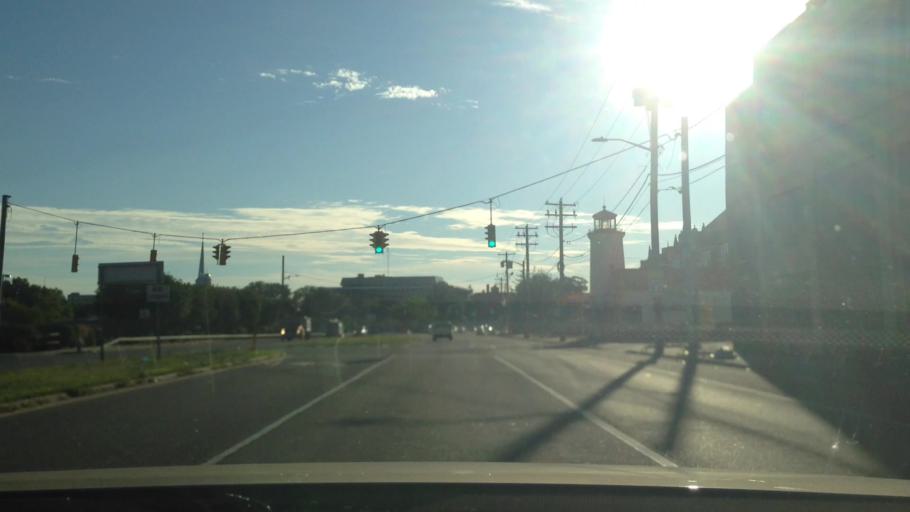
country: US
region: New York
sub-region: Nassau County
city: Hempstead
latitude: 40.7043
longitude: -73.6245
